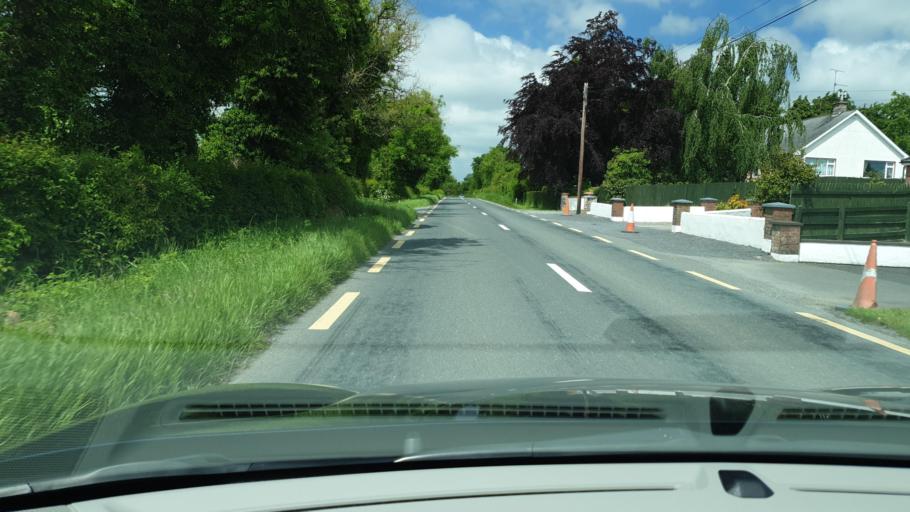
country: IE
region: Ulster
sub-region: An Cabhan
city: Kingscourt
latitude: 53.8924
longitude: -6.7570
